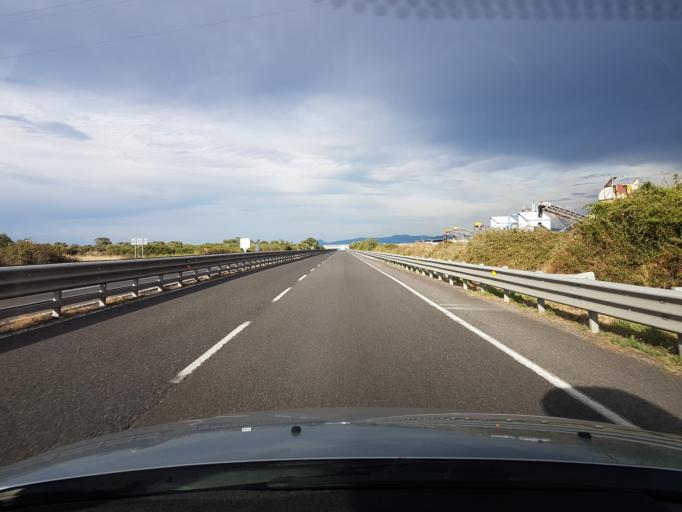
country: IT
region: Sardinia
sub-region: Provincia di Oristano
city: Paulilatino
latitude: 40.0927
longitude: 8.7644
